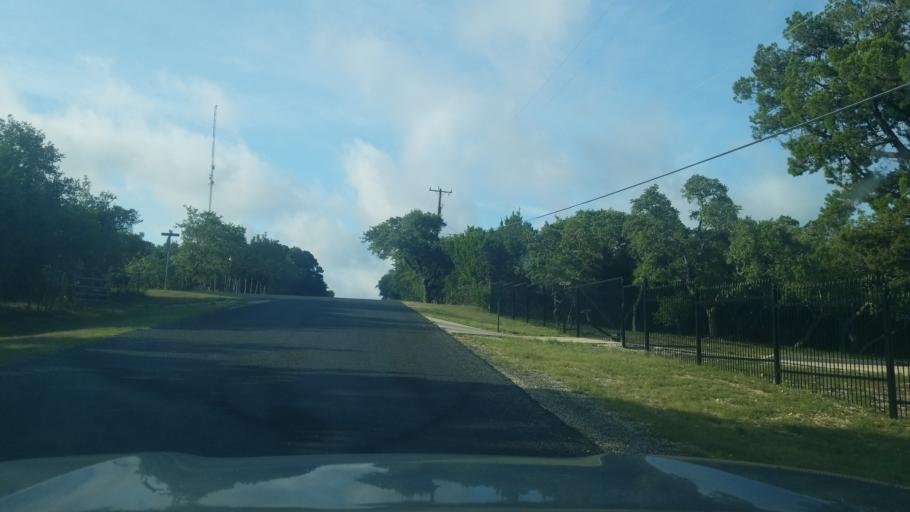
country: US
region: Texas
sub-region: Bexar County
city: Timberwood Park
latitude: 29.7013
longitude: -98.5148
